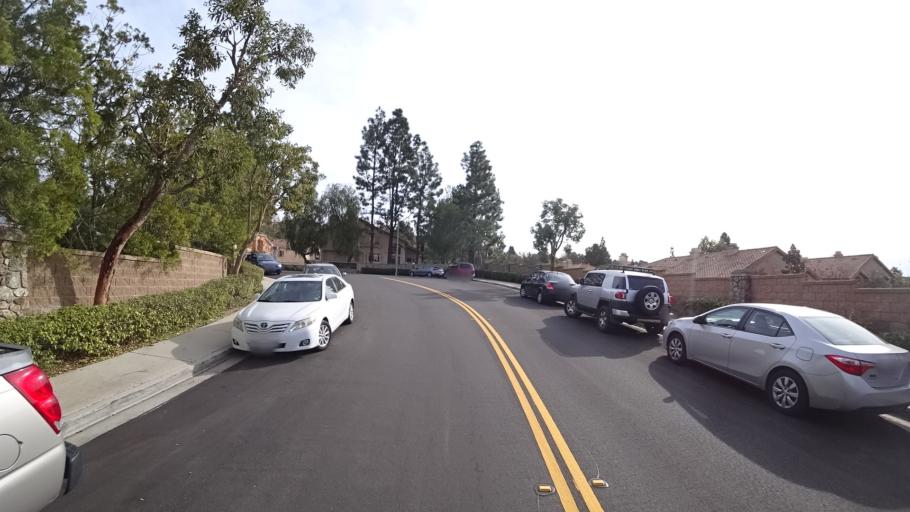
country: US
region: California
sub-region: Orange County
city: Laguna Woods
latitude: 33.6035
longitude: -117.7413
